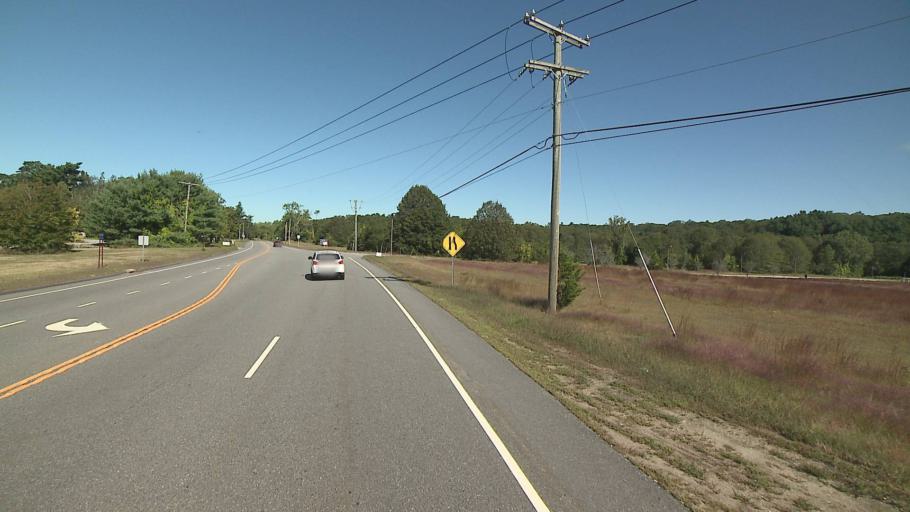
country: US
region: Connecticut
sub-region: New London County
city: Norwich
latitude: 41.4871
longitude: -72.0671
